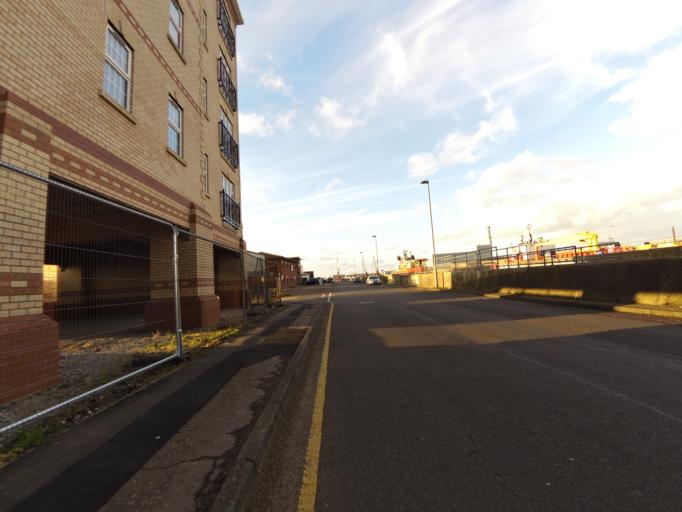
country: GB
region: England
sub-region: Norfolk
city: Gorleston-on-Sea
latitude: 52.5787
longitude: 1.7313
